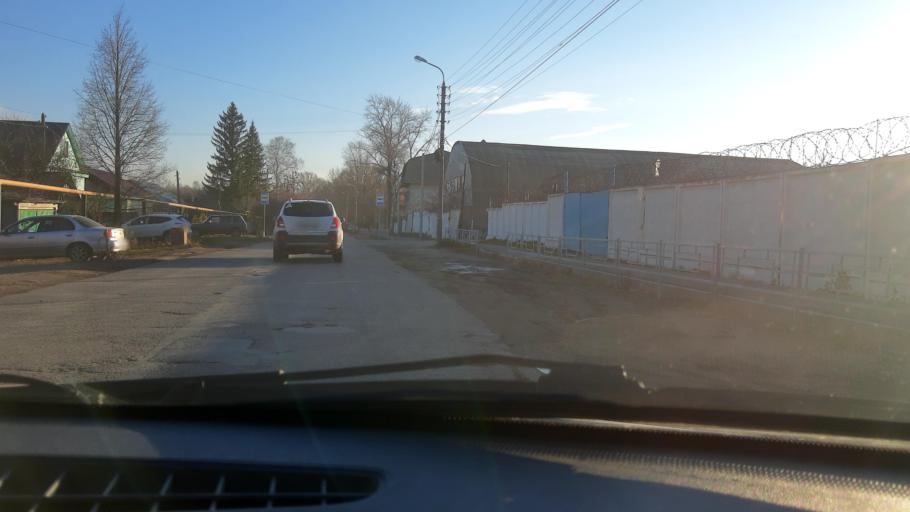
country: RU
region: Bashkortostan
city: Mikhaylovka
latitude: 54.6936
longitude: 55.8493
